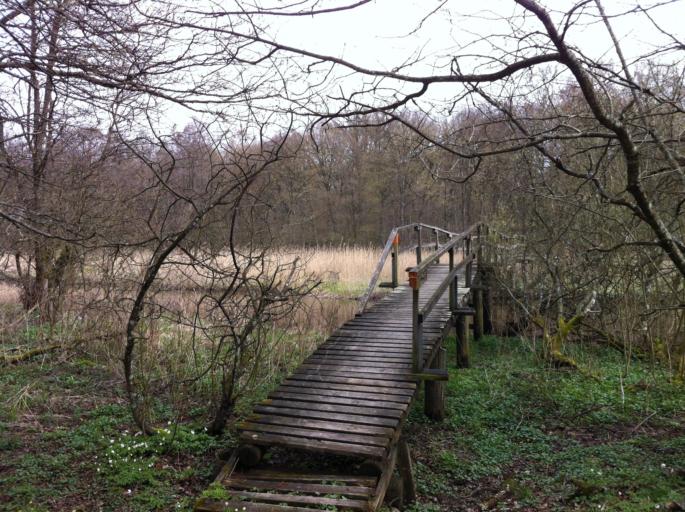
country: SE
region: Skane
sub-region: Eslovs Kommun
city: Stehag
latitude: 56.0131
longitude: 13.3877
